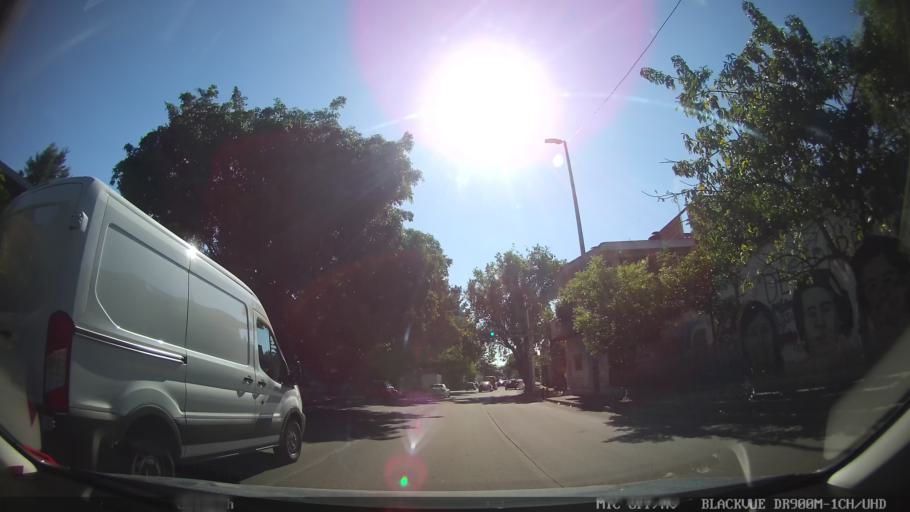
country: MX
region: Jalisco
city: Tlaquepaque
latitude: 20.6645
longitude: -103.3024
